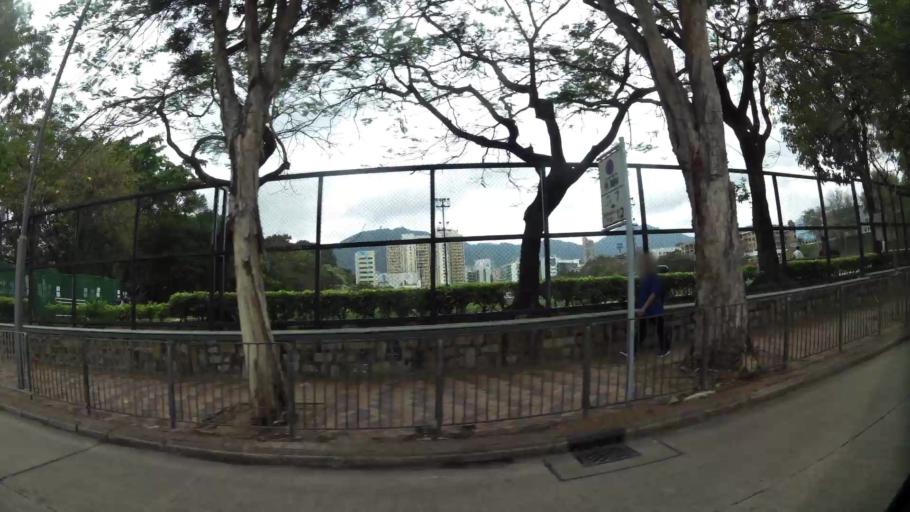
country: HK
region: Sham Shui Po
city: Sham Shui Po
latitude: 22.3267
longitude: 114.1708
